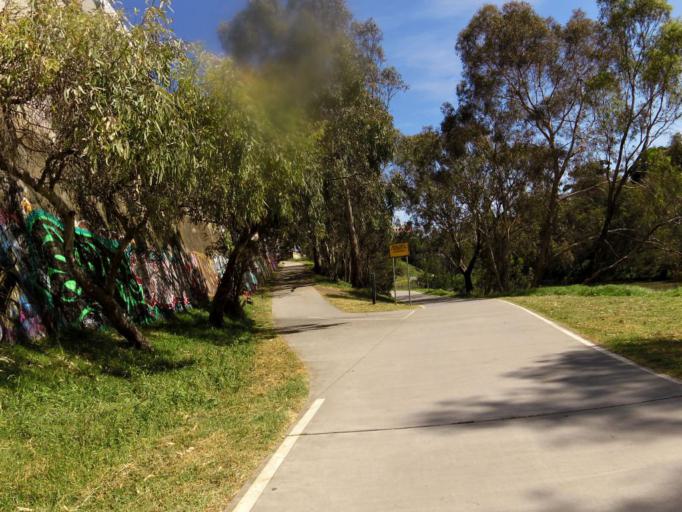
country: AU
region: Victoria
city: Abbotsford
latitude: -37.7992
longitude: 145.0013
